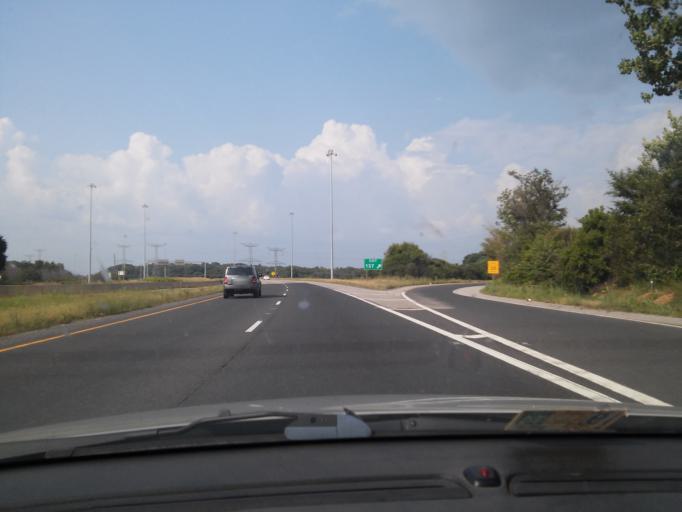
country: US
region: Illinois
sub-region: Will County
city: New Lenox
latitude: 41.5174
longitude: -87.9940
